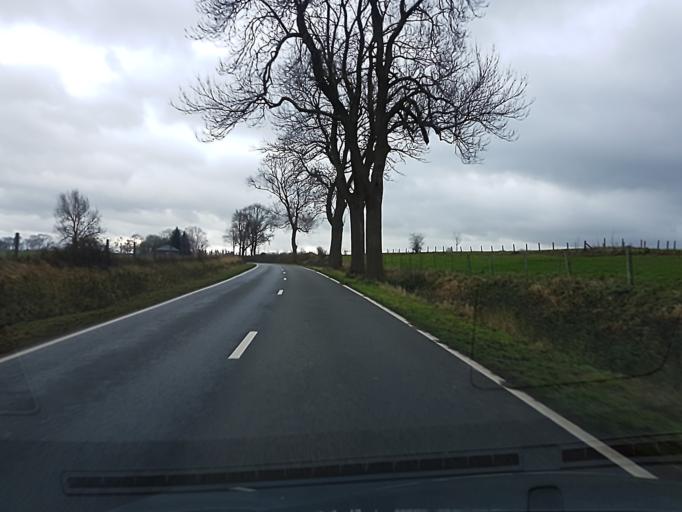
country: BE
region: Wallonia
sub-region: Province de Liege
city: Herve
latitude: 50.6743
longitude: 5.7729
